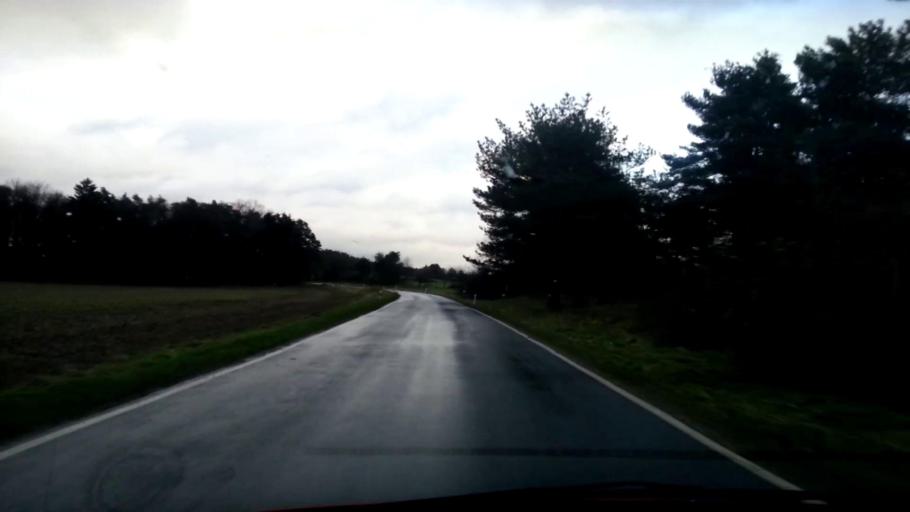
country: DE
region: Bavaria
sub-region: Upper Franconia
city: Aufsess
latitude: 49.9256
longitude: 11.1933
